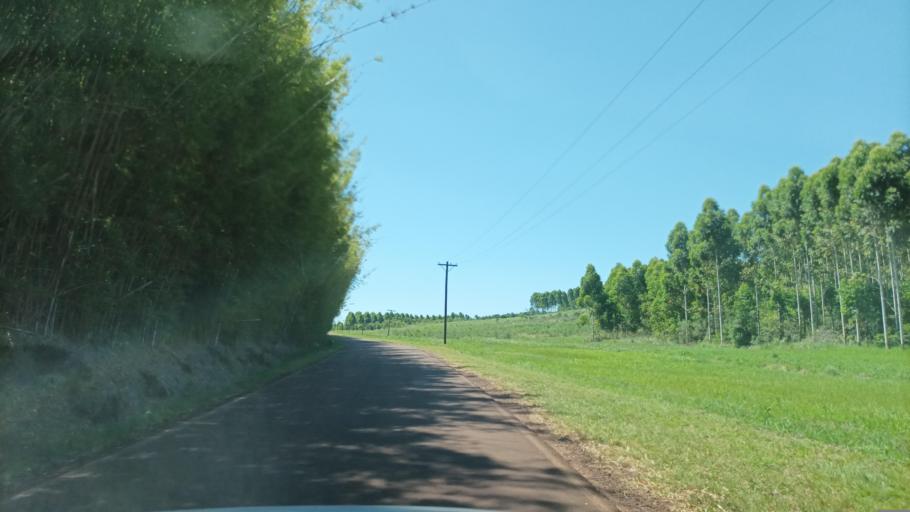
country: AR
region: Misiones
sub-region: Departamento de Apostoles
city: San Jose
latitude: -27.7818
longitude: -55.7229
